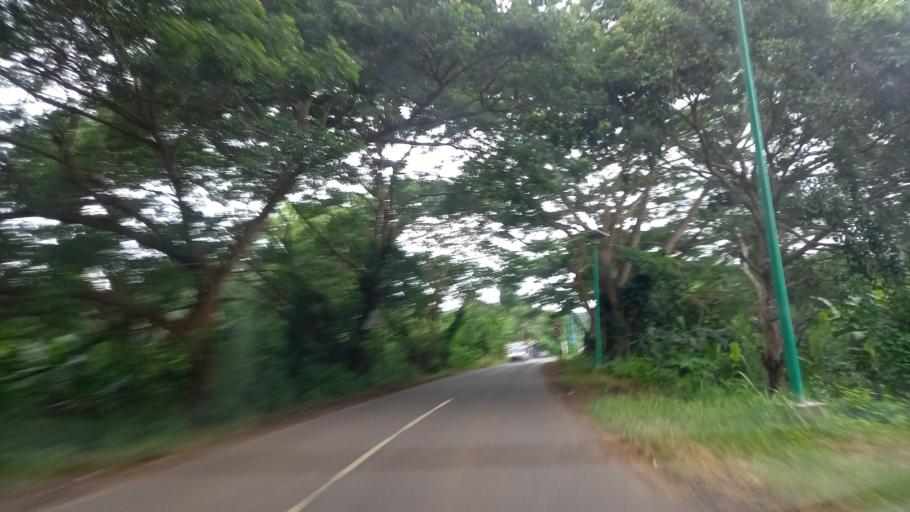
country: YT
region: Chirongui
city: Chirongui
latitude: -12.9174
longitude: 45.1593
